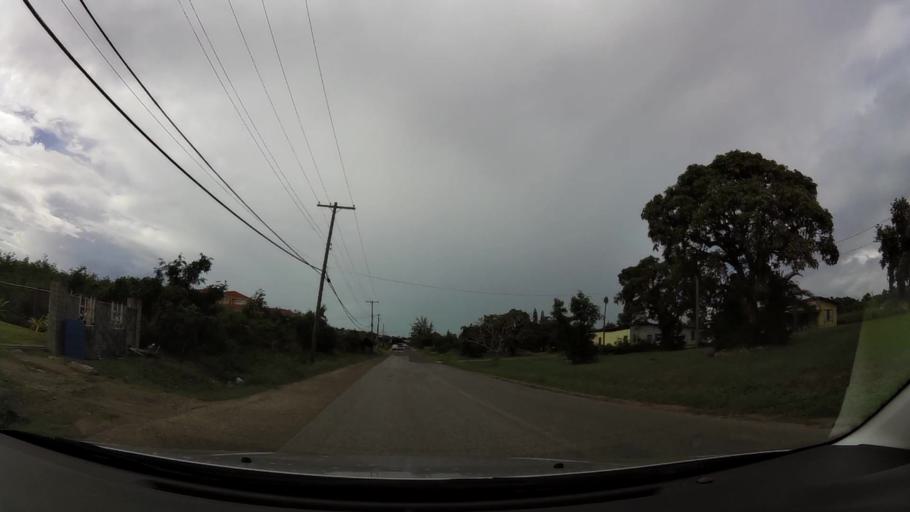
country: AG
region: Saint John
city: Potters Village
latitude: 17.0880
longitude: -61.8128
